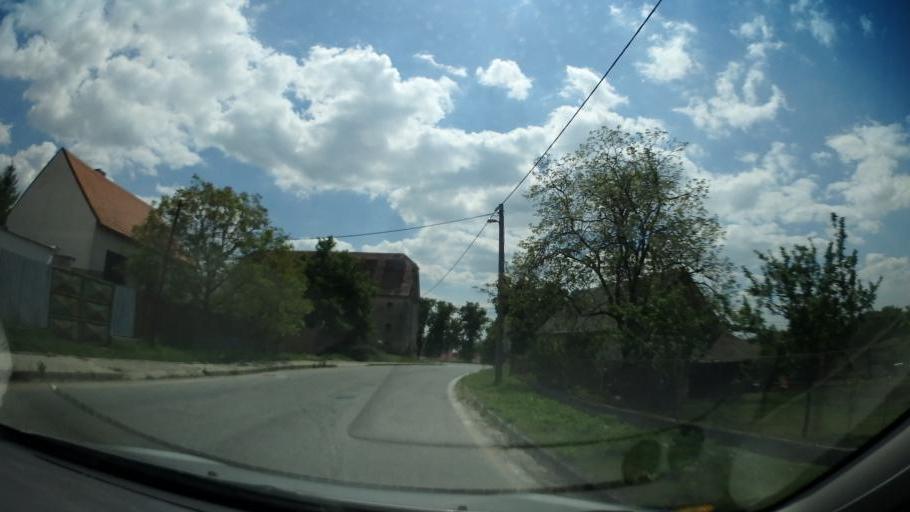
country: CZ
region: Vysocina
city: Hrotovice
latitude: 49.1326
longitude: 16.0800
